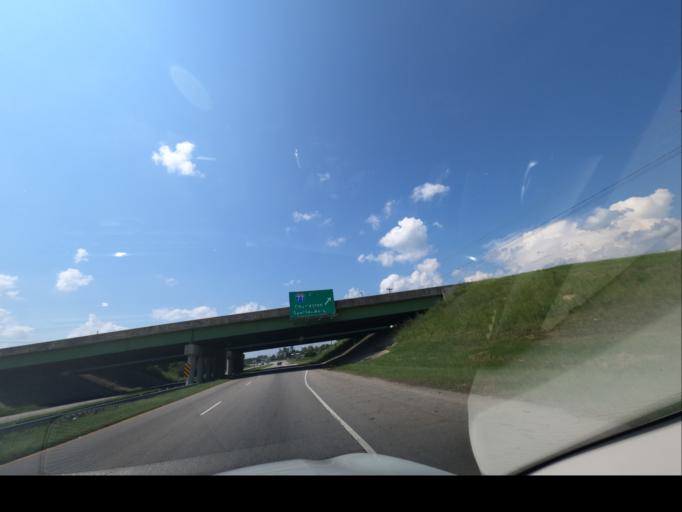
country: US
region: South Carolina
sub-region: Richland County
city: Columbia
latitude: 33.9501
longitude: -80.9900
